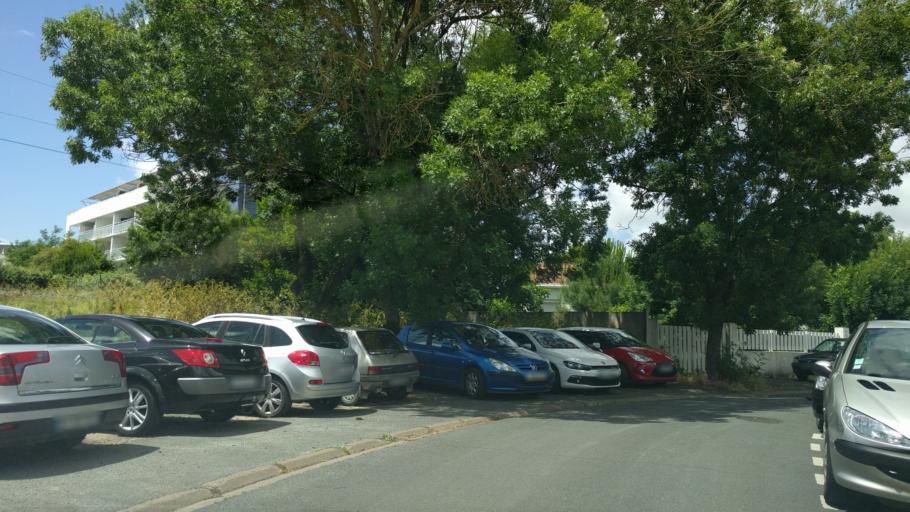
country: FR
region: Poitou-Charentes
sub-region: Departement de la Charente-Maritime
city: La Rochelle
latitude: 46.1585
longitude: -1.1395
